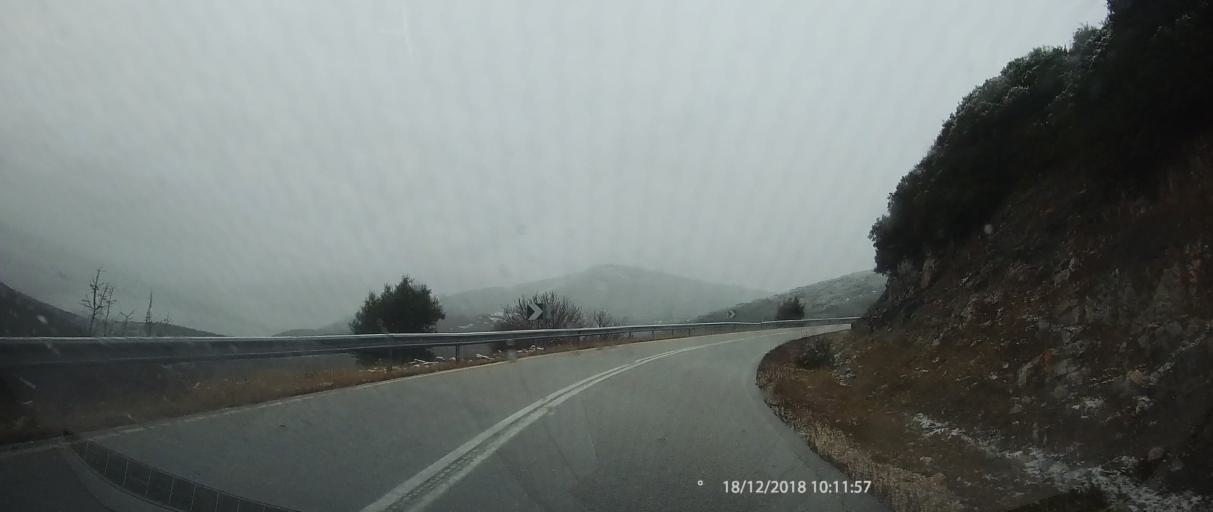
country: GR
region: Thessaly
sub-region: Nomos Larisis
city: Livadi
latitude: 40.0941
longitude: 22.2063
